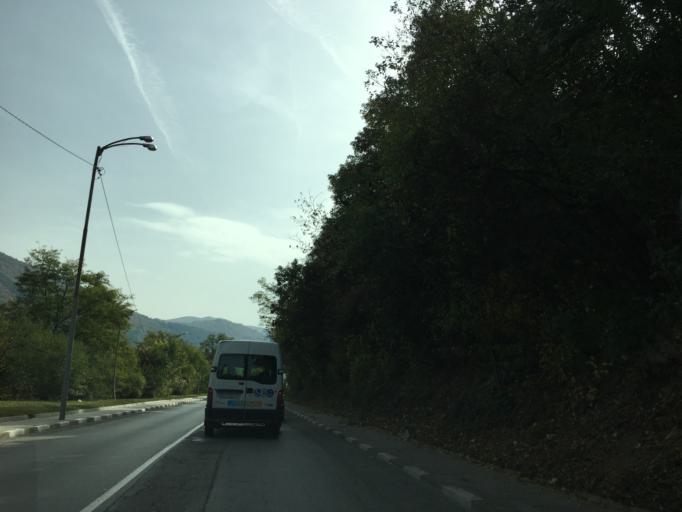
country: BG
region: Sofia-Capital
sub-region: Stolichna Obshtina
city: Sofia
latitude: 42.5934
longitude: 23.4163
